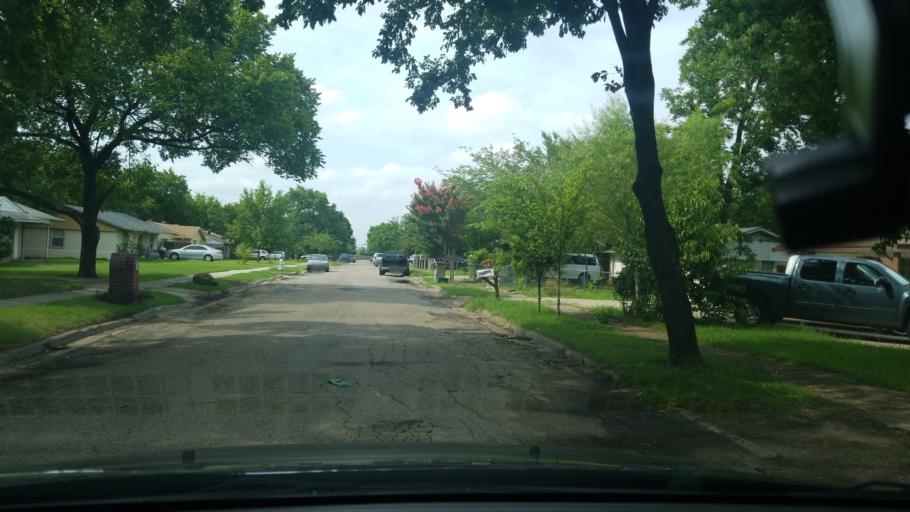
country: US
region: Texas
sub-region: Dallas County
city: Mesquite
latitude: 32.7579
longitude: -96.6268
